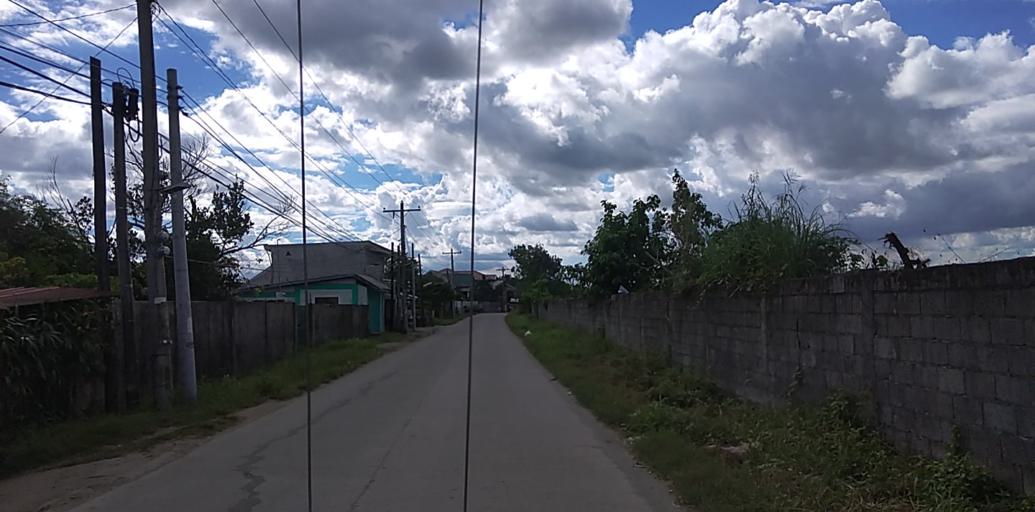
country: PH
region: Central Luzon
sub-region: Province of Pampanga
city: Arayat
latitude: 15.1400
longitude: 120.7780
